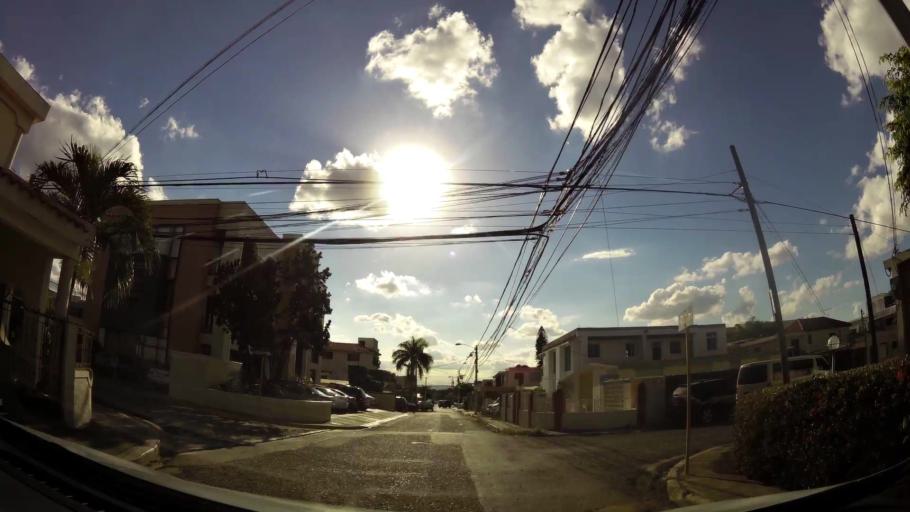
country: DO
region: Santiago
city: Santiago de los Caballeros
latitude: 19.4617
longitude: -70.6907
